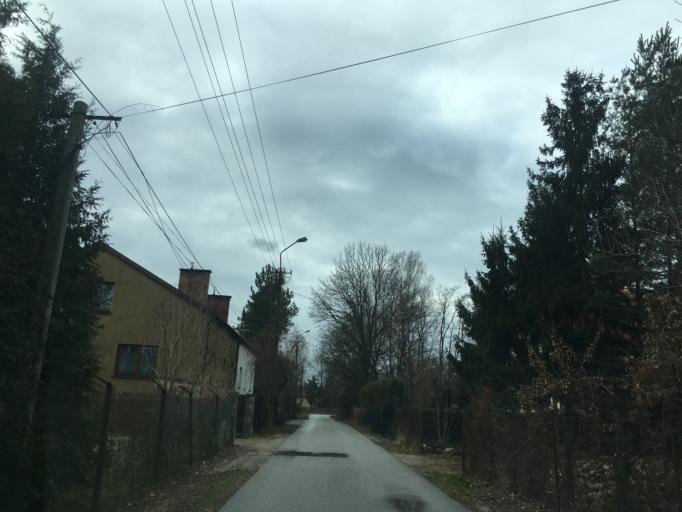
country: PL
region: Masovian Voivodeship
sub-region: Powiat piaseczynski
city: Lesznowola
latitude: 52.0343
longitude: 20.9613
